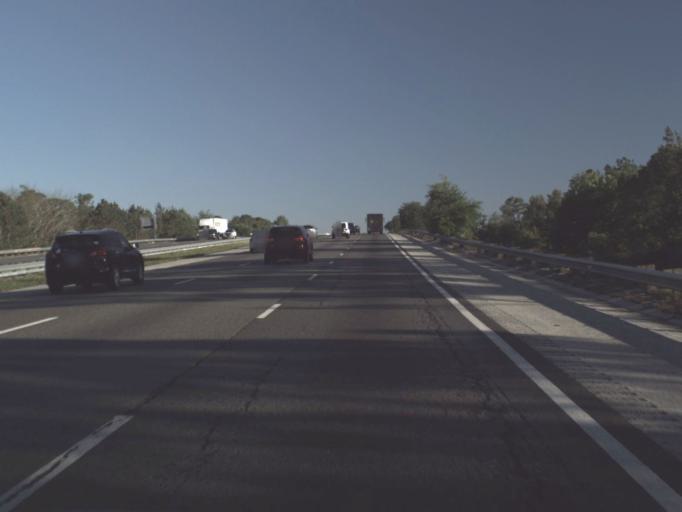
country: US
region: Florida
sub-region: Flagler County
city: Flagler Beach
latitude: 29.5000
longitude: -81.1931
